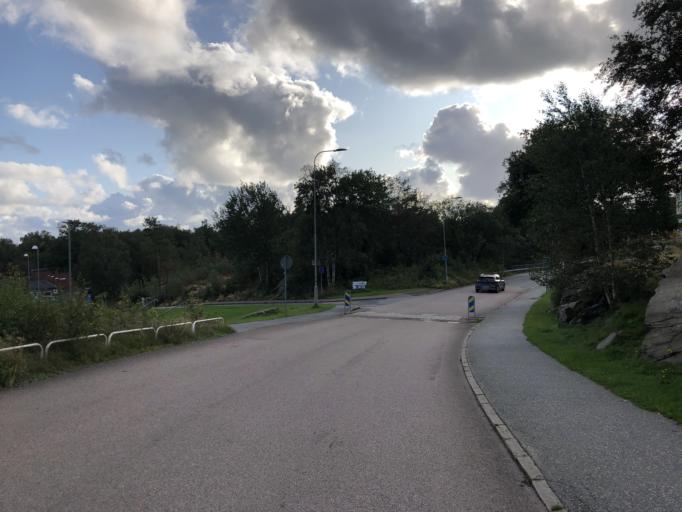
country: SE
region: Vaestra Goetaland
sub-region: Goteborg
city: Majorna
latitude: 57.7312
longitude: 11.8934
